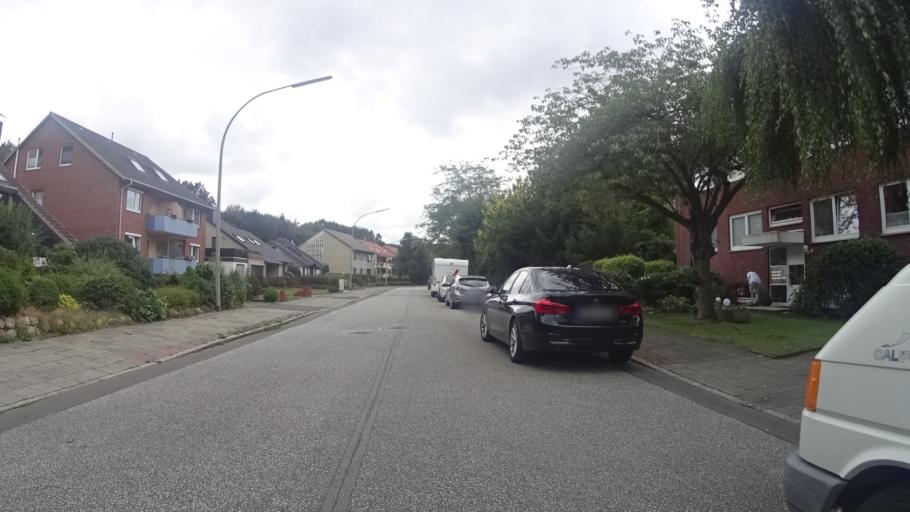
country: DE
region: Bremen
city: Bremerhaven
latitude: 53.5326
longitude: 8.6108
